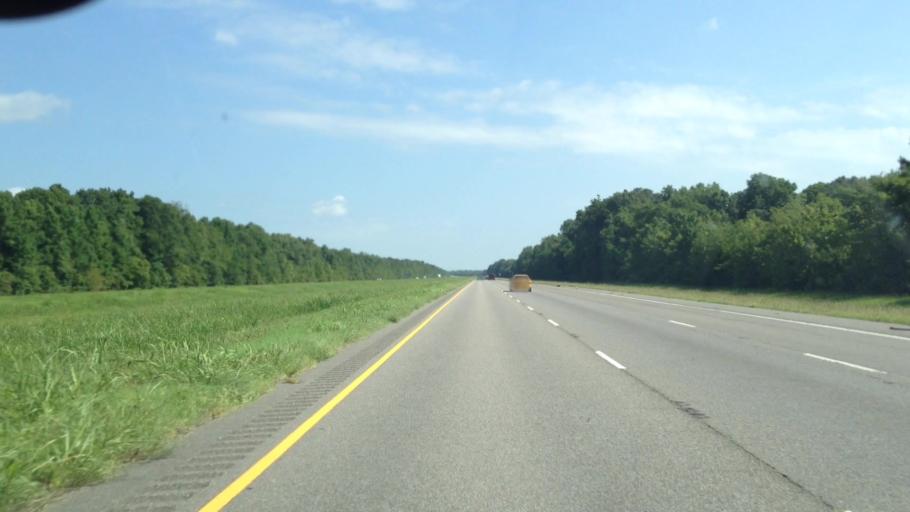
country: US
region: Louisiana
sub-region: Avoyelles Parish
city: Bunkie
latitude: 30.8709
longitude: -92.2275
